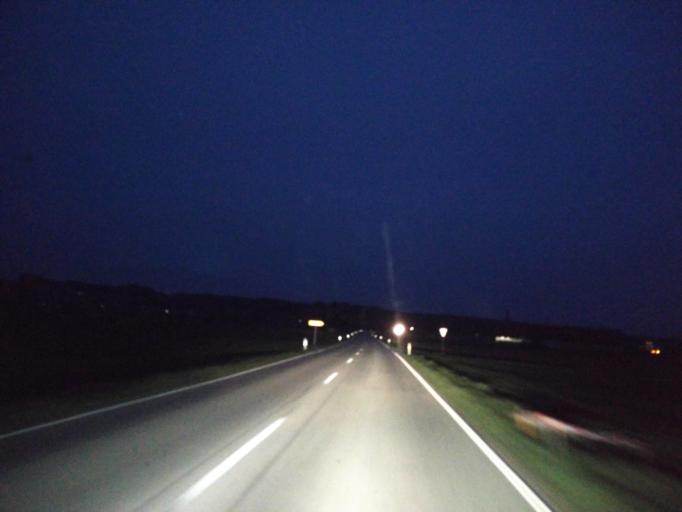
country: DE
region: Bavaria
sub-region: Upper Bavaria
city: Halfing
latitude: 47.9574
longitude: 12.2667
